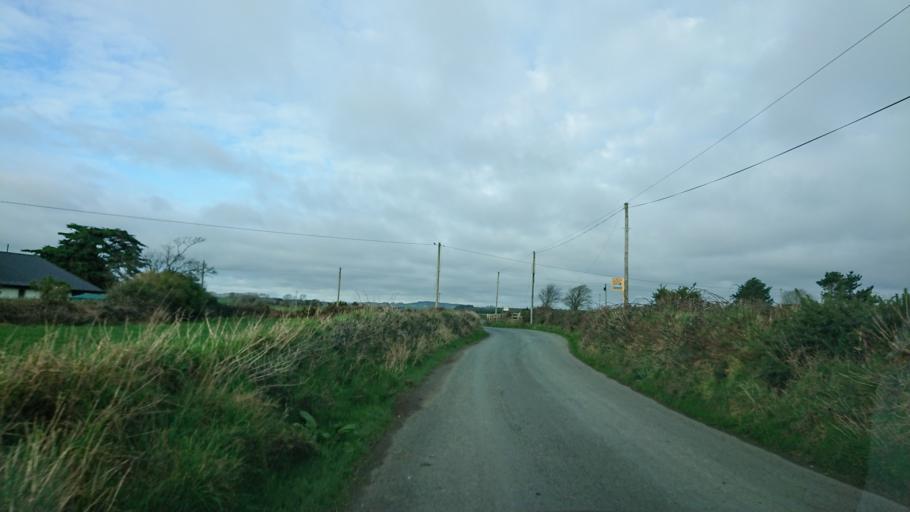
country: IE
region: Munster
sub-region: Waterford
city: Portlaw
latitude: 52.1506
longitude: -7.3093
